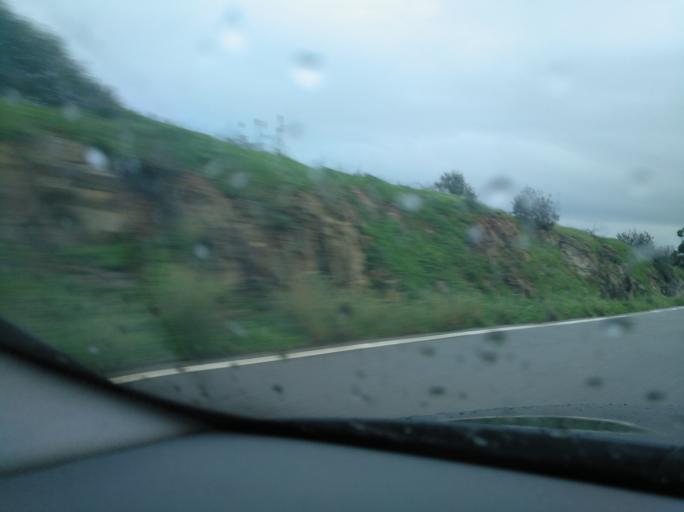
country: PT
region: Beja
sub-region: Mertola
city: Mertola
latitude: 37.5597
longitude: -7.6618
